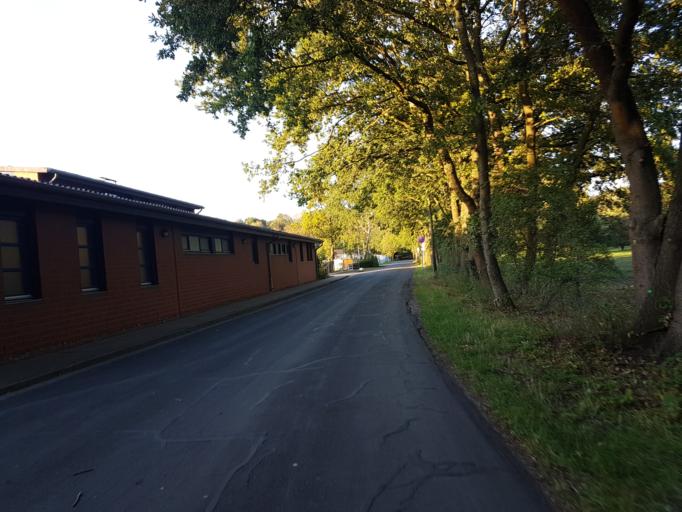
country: DE
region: Lower Saxony
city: Langenhagen
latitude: 52.4412
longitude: 9.7663
